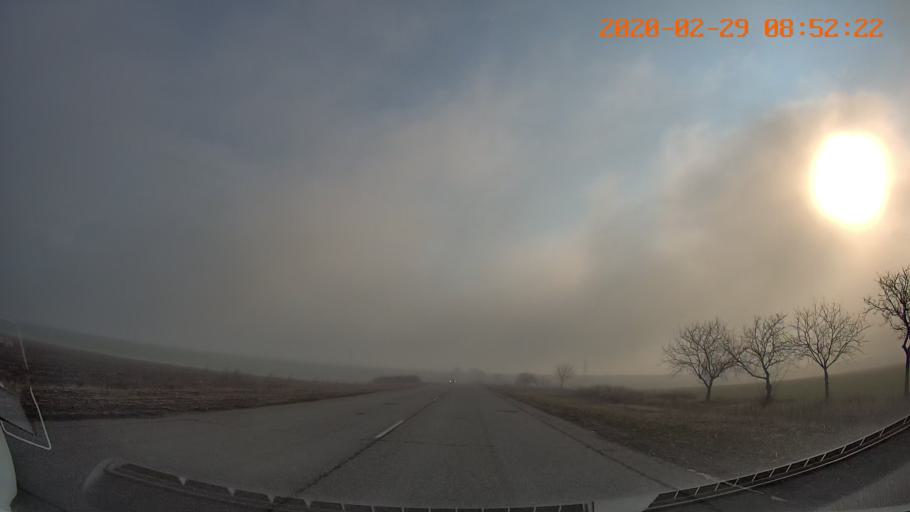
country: MD
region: Anenii Noi
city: Varnita
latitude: 46.9234
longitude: 29.5366
